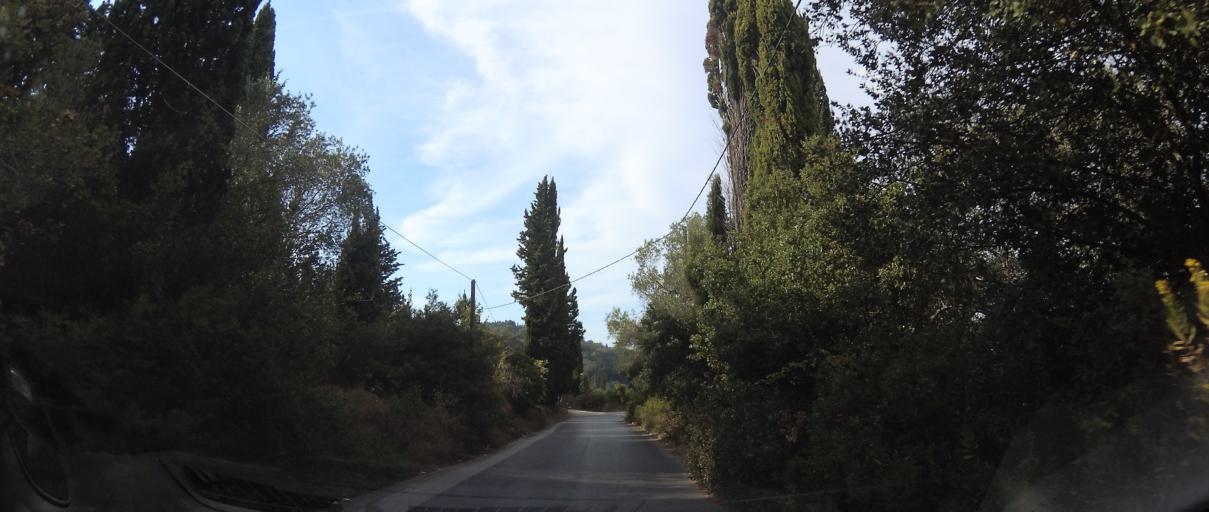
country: GR
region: Ionian Islands
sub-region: Nomos Kerkyras
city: Kynopiastes
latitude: 39.5576
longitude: 19.8564
